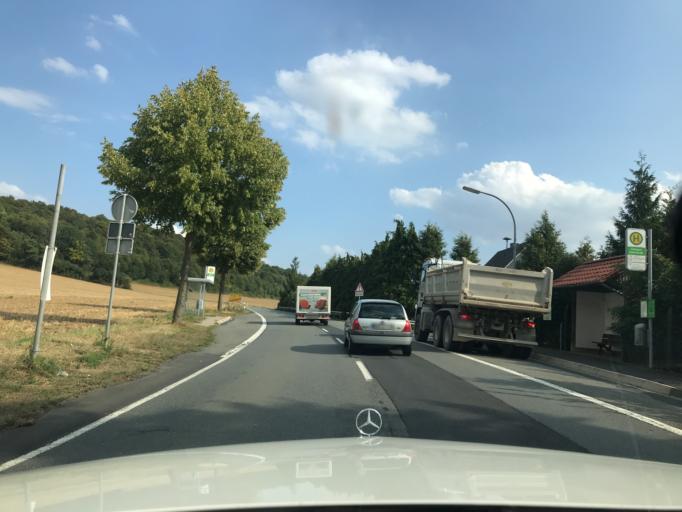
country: DE
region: Lower Saxony
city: Adelebsen
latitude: 51.5933
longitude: 9.7863
